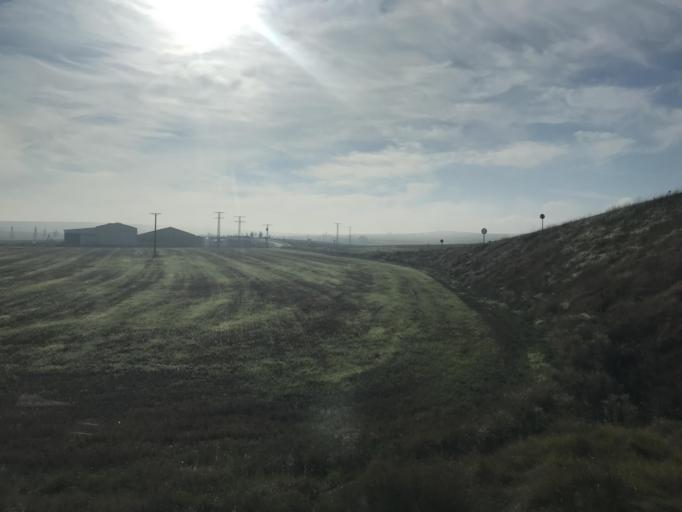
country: ES
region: Castille and Leon
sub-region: Provincia de Burgos
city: Grisalena
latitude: 42.6063
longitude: -3.2786
